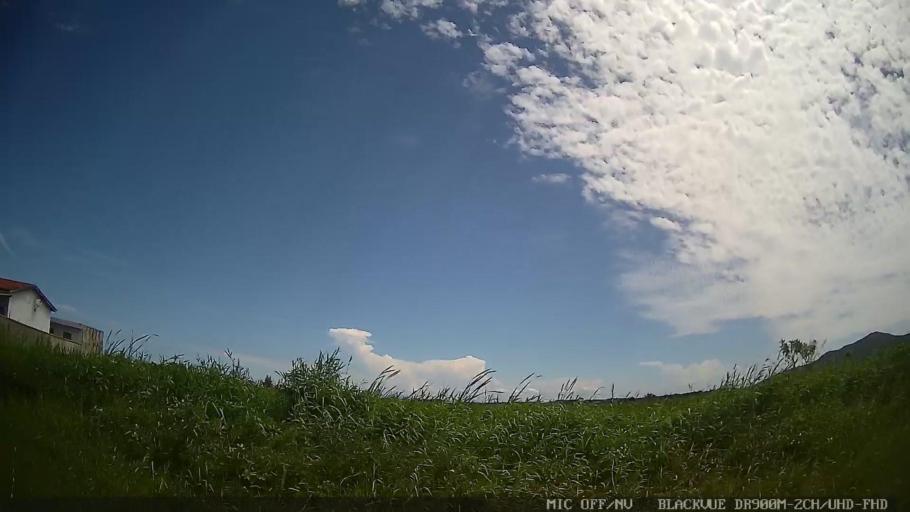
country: BR
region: Sao Paulo
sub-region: Iguape
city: Iguape
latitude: -24.7210
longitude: -47.5072
